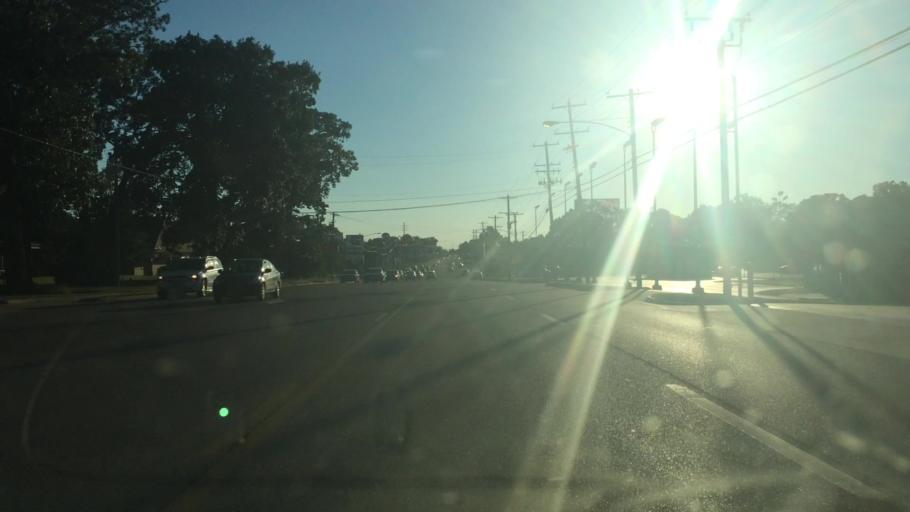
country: US
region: Missouri
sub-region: Greene County
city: Springfield
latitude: 37.1809
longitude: -93.2410
